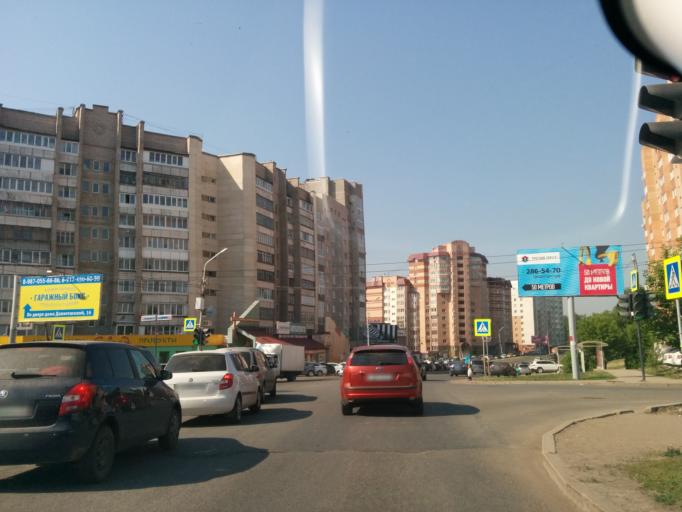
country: RU
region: Bashkortostan
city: Ufa
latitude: 54.7373
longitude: 55.9897
